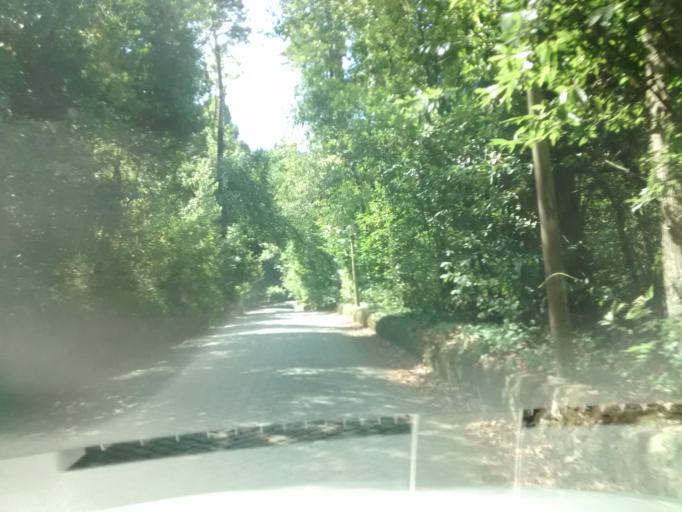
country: PT
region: Aveiro
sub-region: Mealhada
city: Pampilhosa do Botao
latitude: 40.3775
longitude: -8.3612
